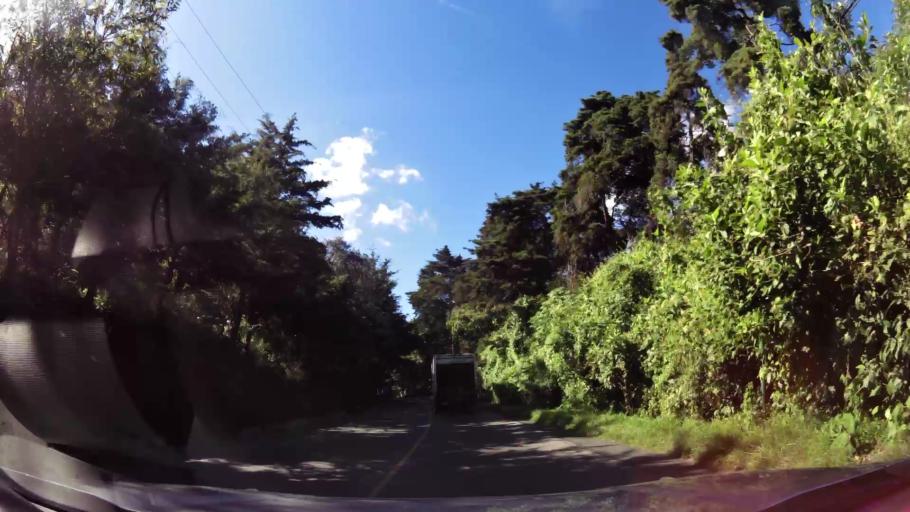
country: GT
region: Sacatepequez
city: Santa Lucia Milpas Altas
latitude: 14.5810
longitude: -90.6537
